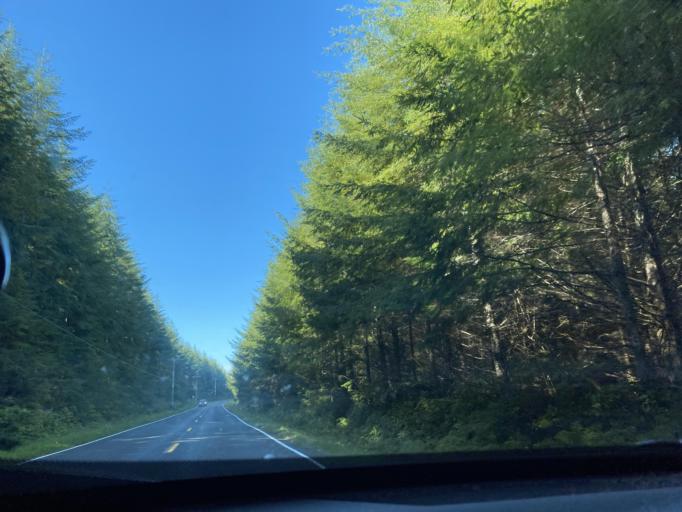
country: US
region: Washington
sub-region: Clallam County
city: Forks
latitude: 47.9471
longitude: -124.4902
